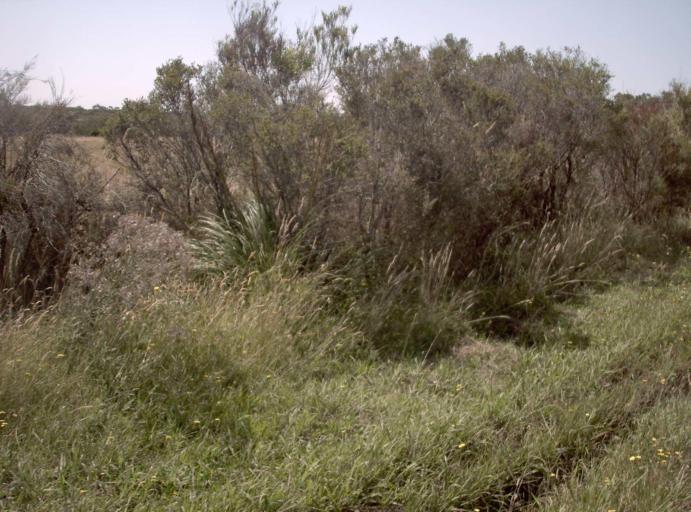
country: AU
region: Victoria
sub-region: Bass Coast
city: North Wonthaggi
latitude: -38.5946
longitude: 145.7254
